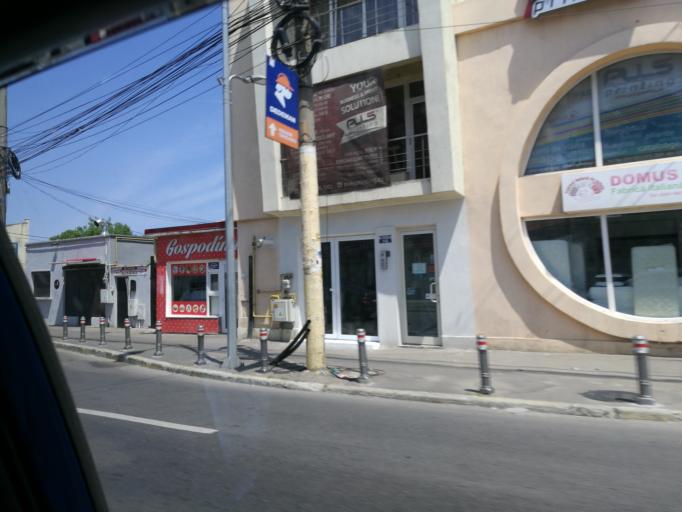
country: RO
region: Constanta
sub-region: Municipiul Constanta
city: Constanta
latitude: 44.1970
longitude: 28.6483
